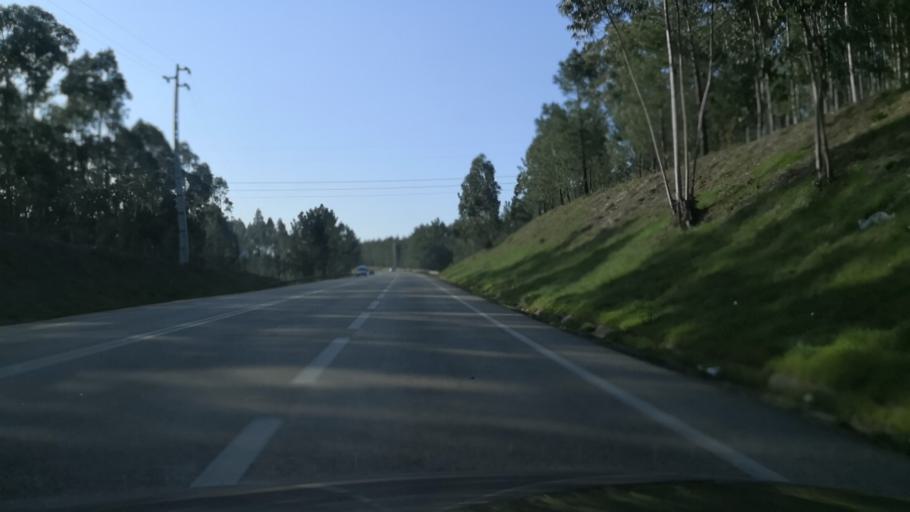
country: PT
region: Leiria
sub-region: Leiria
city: Leiria
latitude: 39.7464
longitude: -8.8529
